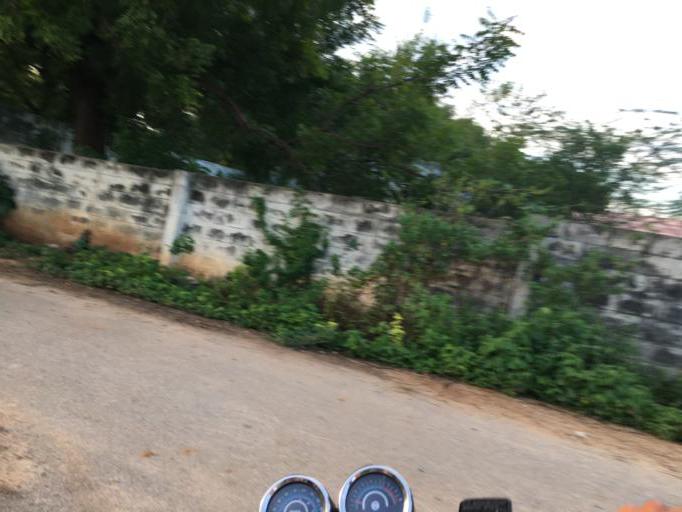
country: IN
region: Telangana
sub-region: Nalgonda
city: Nalgonda
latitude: 17.1741
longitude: 79.4180
